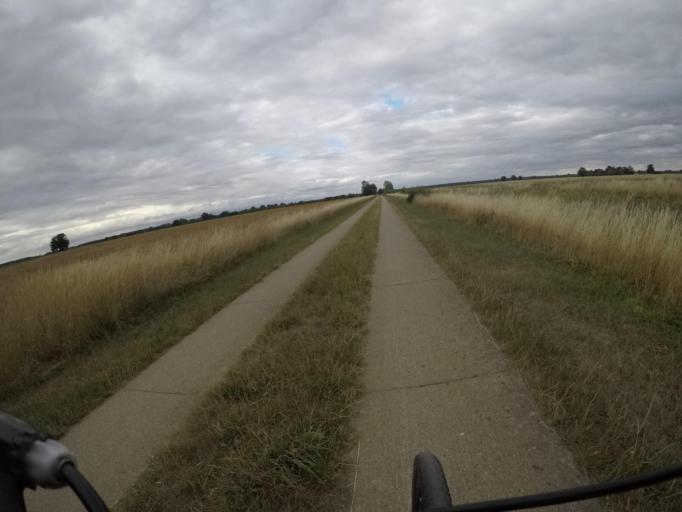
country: DE
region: Lower Saxony
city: Neu Darchau
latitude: 53.2460
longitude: 10.9147
